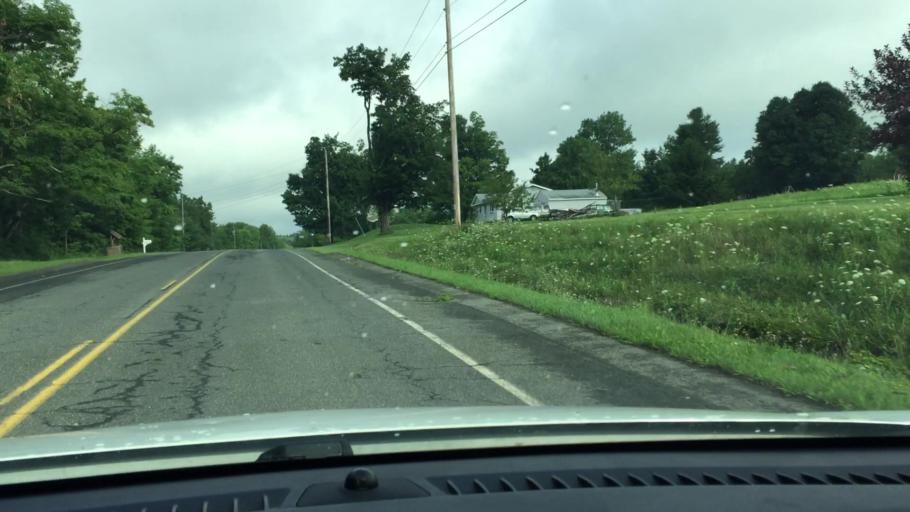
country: US
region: Massachusetts
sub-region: Berkshire County
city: Hinsdale
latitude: 42.4309
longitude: -73.0135
